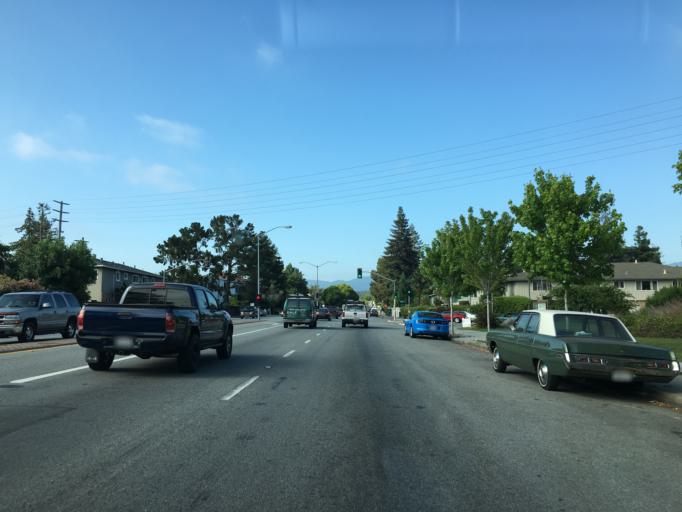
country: US
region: California
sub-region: San Mateo County
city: Redwood City
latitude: 37.4604
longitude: -122.2258
